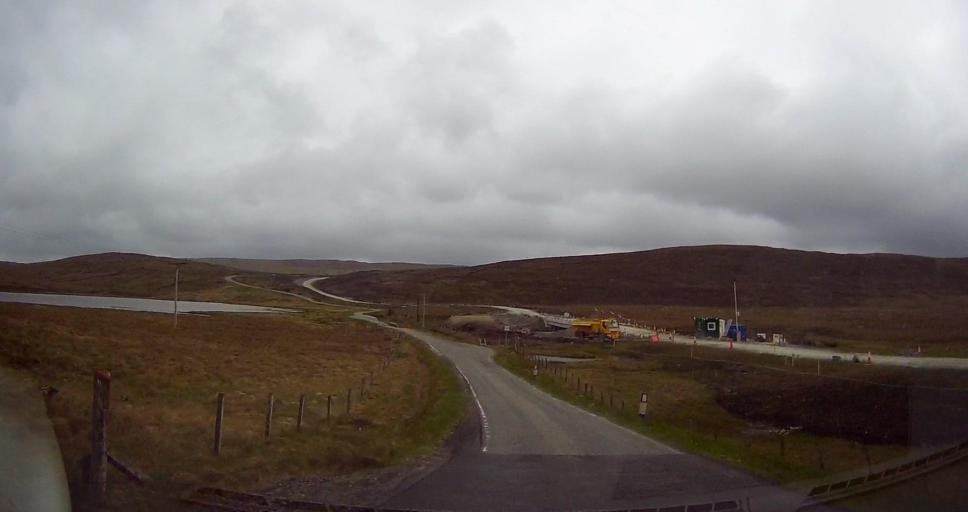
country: GB
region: Scotland
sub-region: Shetland Islands
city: Lerwick
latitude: 60.2797
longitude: -1.2479
